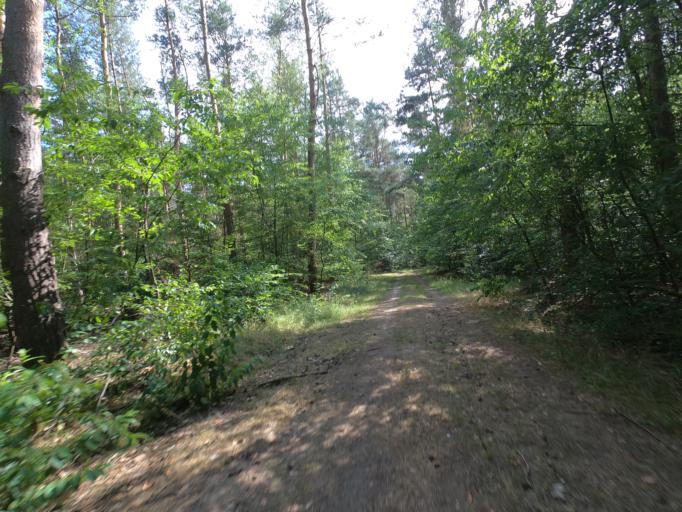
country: DE
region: Hesse
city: Morfelden-Walldorf
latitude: 50.0265
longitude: 8.6100
